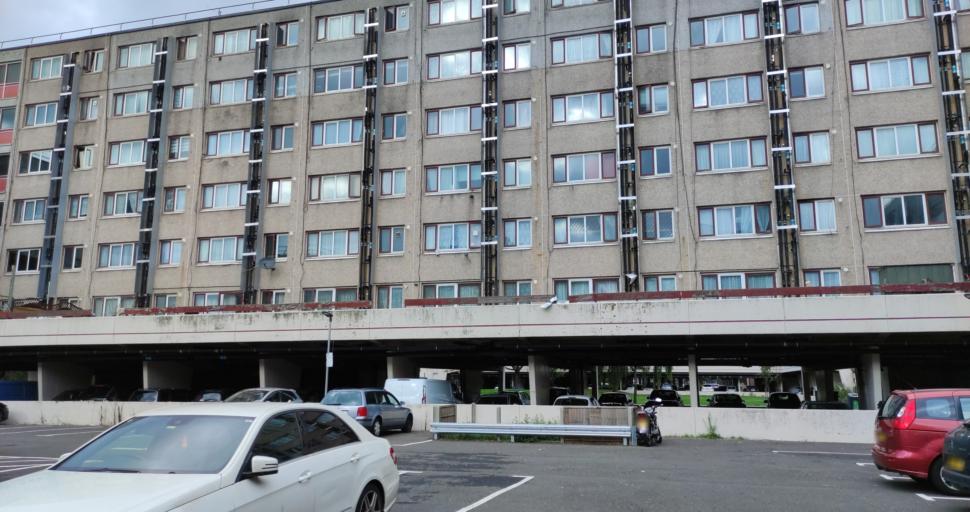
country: GB
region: England
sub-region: Greater London
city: Harringay
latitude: 51.5940
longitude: -0.0833
